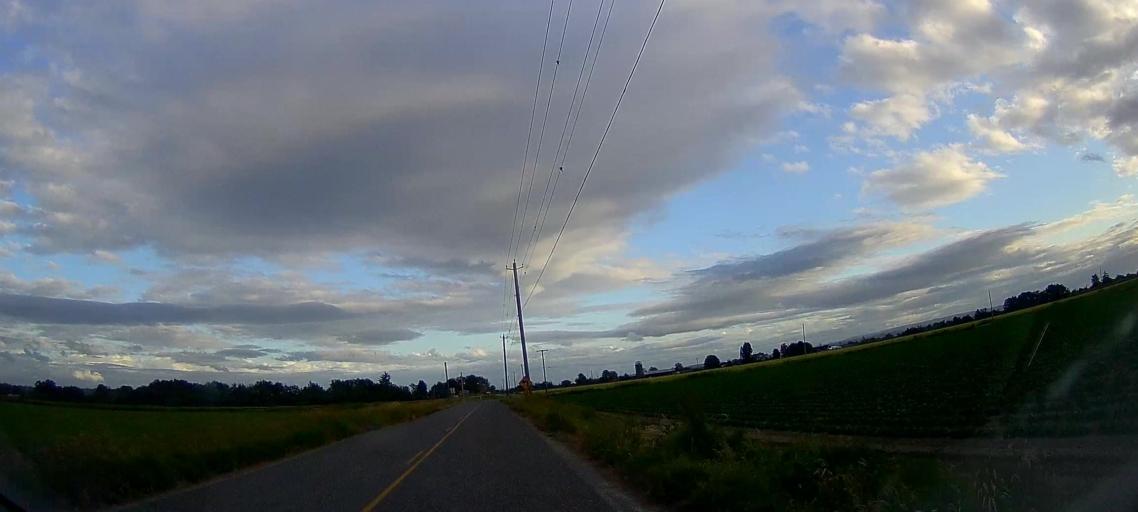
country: US
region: Washington
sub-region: Snohomish County
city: Stanwood
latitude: 48.3312
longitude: -122.3787
